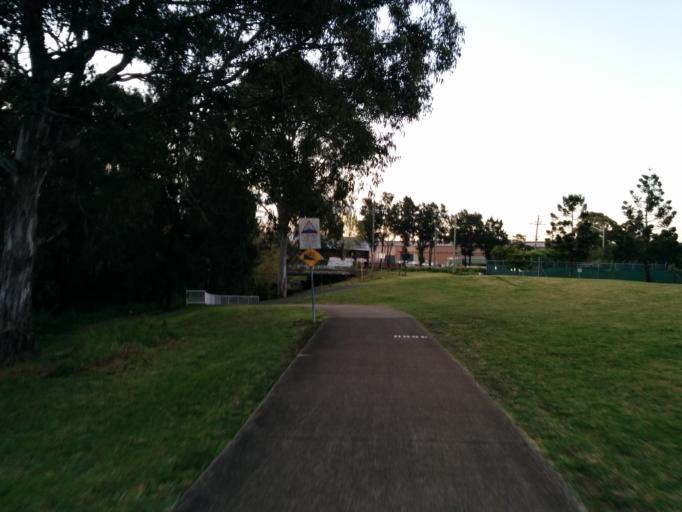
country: AU
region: New South Wales
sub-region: Fairfield
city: Fairfield Heights
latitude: -33.8509
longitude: 150.9454
